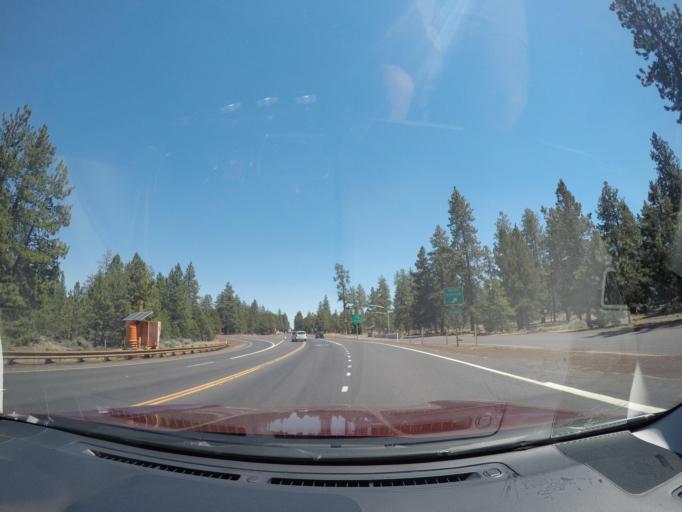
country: US
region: Oregon
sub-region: Deschutes County
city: Sisters
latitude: 44.2881
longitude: -121.5409
